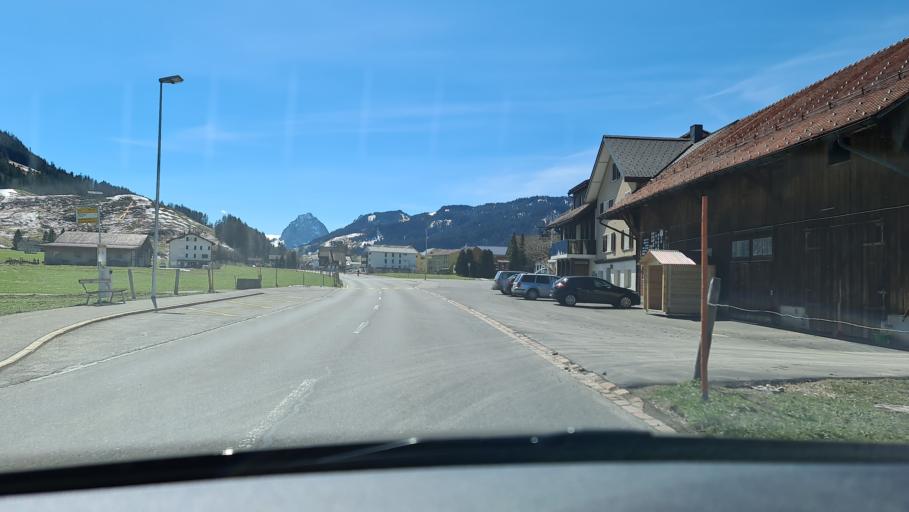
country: CH
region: Schwyz
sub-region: Bezirk Einsiedeln
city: Einsiedeln
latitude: 47.1169
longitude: 8.7377
